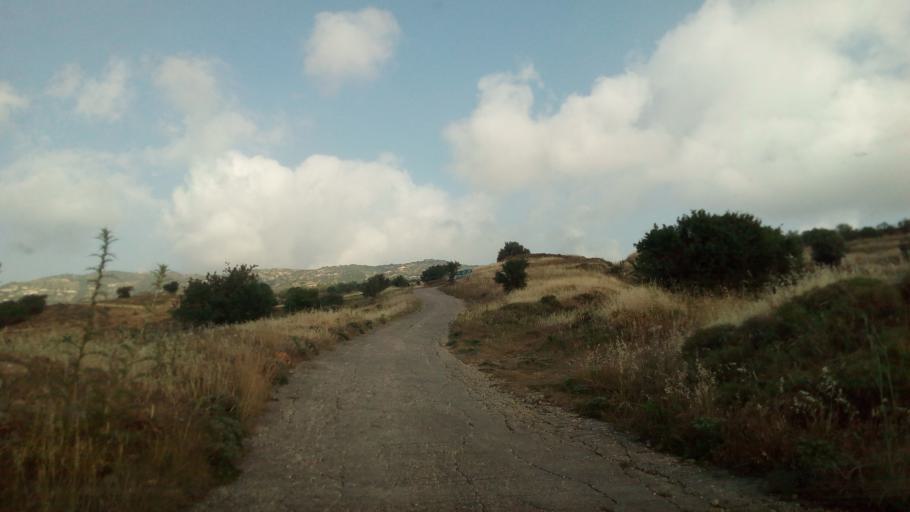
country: CY
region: Limassol
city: Pachna
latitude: 34.8162
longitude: 32.6403
